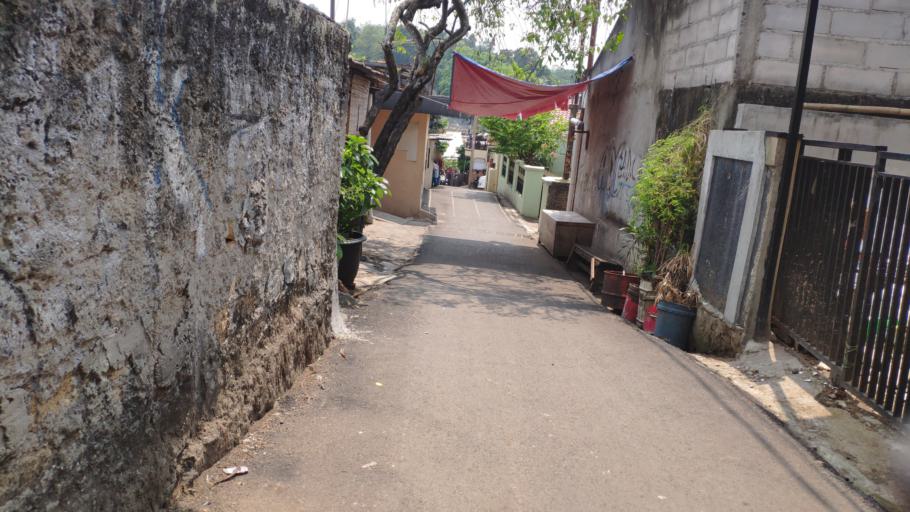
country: ID
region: West Java
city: Pamulang
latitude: -6.3069
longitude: 106.8156
